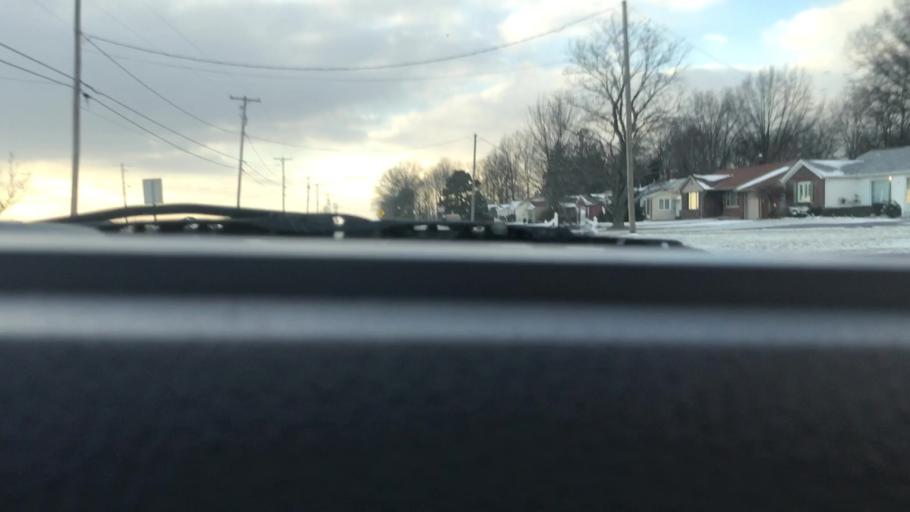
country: US
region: Ohio
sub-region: Mahoning County
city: Canfield
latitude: 41.0440
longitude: -80.7565
